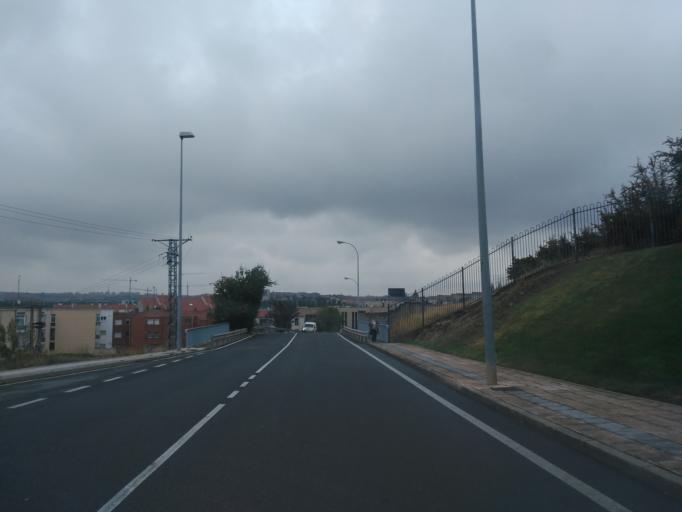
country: ES
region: Castille and Leon
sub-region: Provincia de Salamanca
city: Salamanca
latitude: 40.9536
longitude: -5.6798
